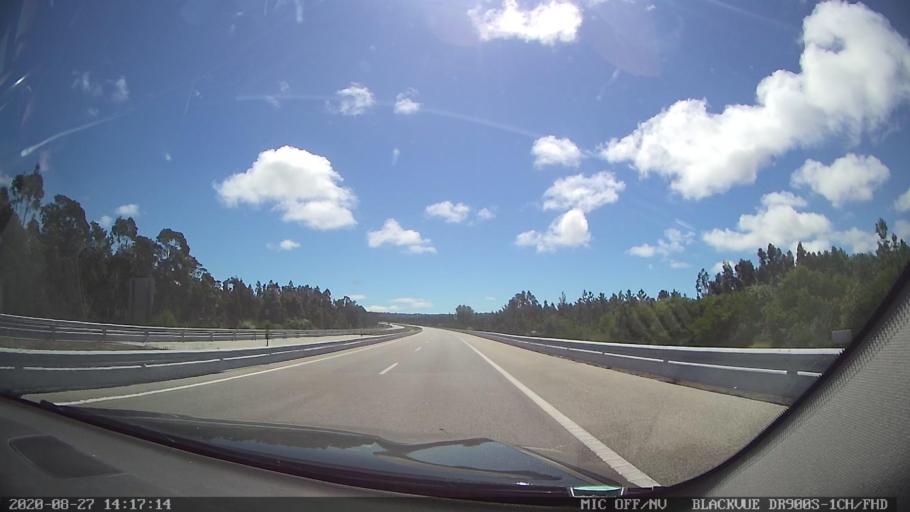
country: PT
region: Coimbra
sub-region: Figueira da Foz
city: Alhadas
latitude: 40.2066
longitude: -8.8141
